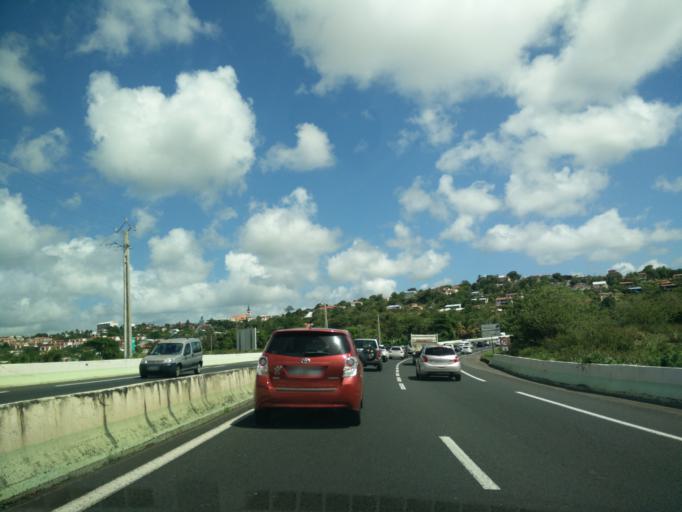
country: MQ
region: Martinique
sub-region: Martinique
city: Ducos
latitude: 14.5845
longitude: -60.9800
